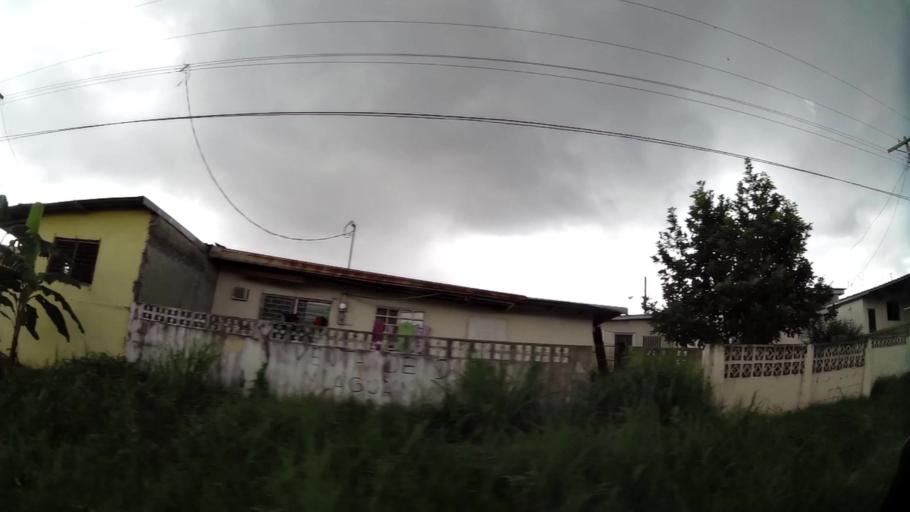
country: PA
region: Panama
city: San Miguelito
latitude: 9.0538
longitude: -79.4422
